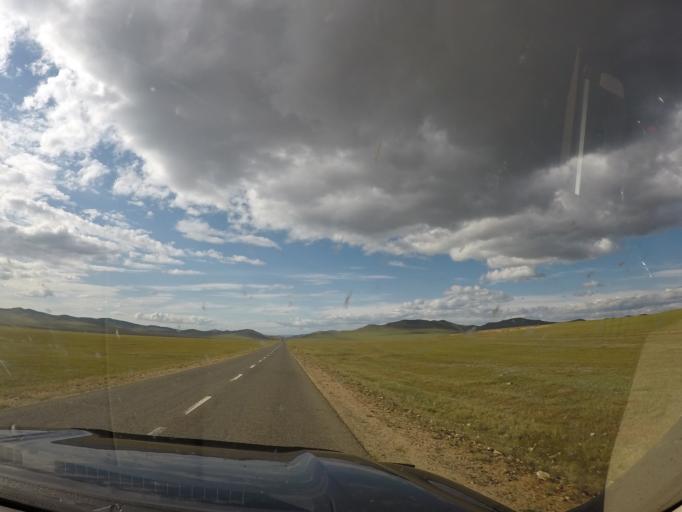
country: MN
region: Hentiy
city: Modot
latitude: 47.6376
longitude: 109.1589
